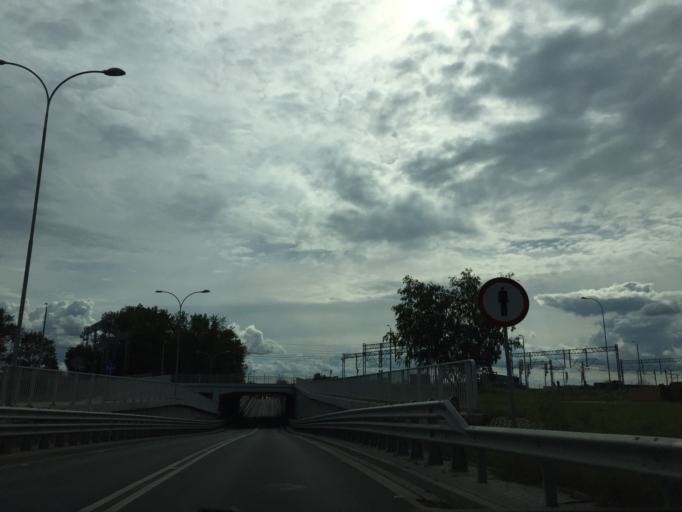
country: PL
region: Lublin Voivodeship
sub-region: Powiat lukowski
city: Lukow
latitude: 51.9385
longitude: 22.4010
